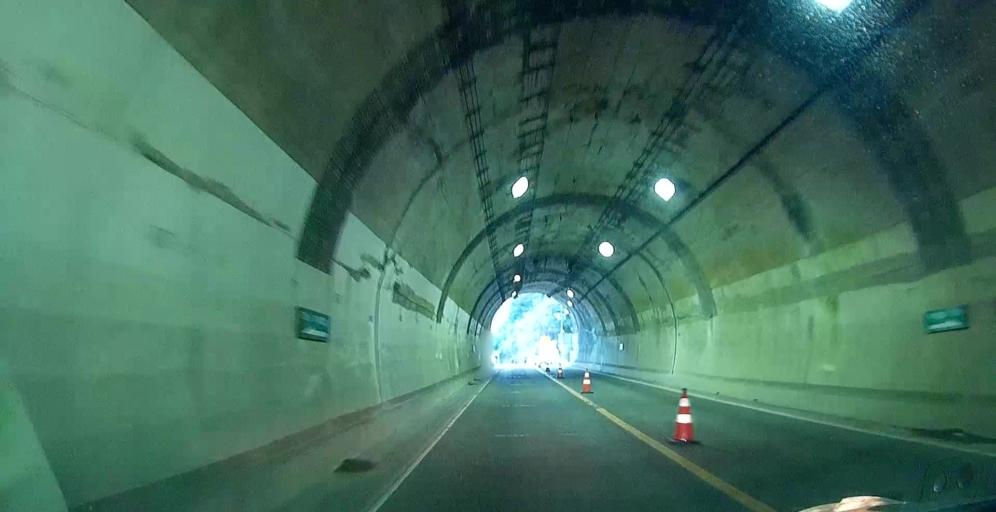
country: JP
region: Kumamoto
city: Yatsushiro
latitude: 32.3736
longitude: 130.5341
